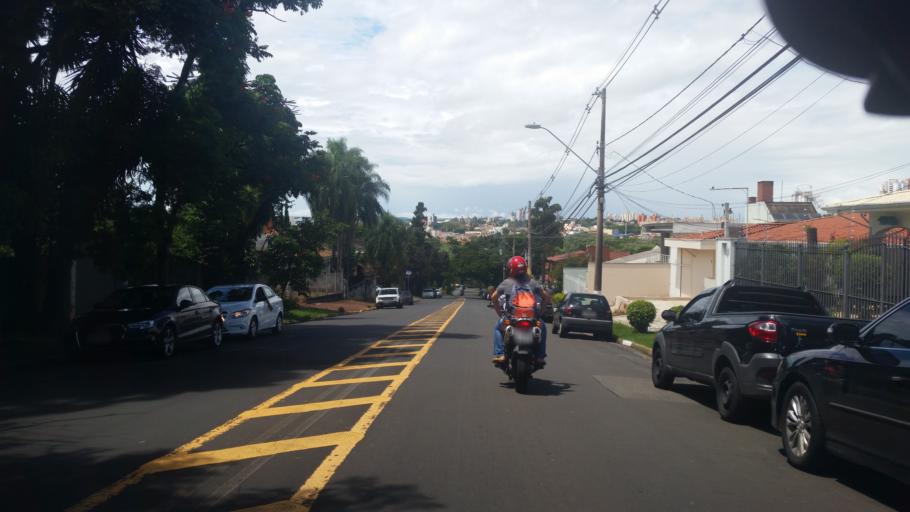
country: BR
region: Sao Paulo
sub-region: Campinas
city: Campinas
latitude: -22.8700
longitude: -47.0506
